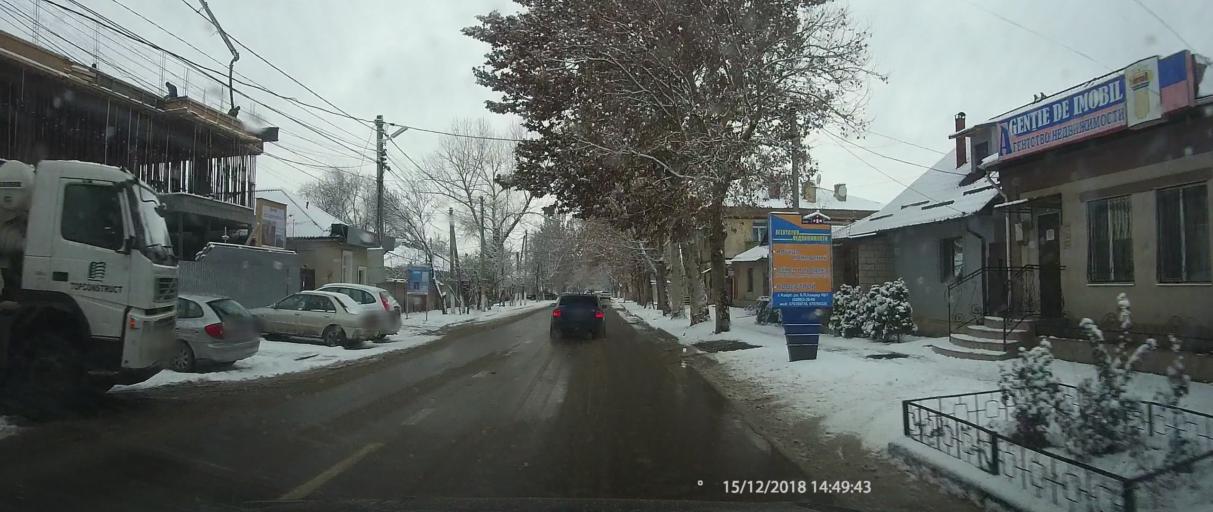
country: MD
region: Cahul
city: Cahul
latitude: 45.9027
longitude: 28.1949
